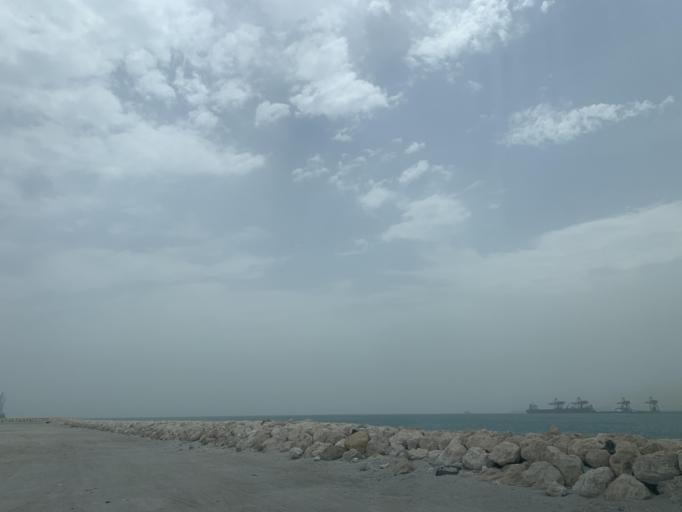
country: BH
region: Muharraq
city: Al Hadd
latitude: 26.2089
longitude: 50.6987
